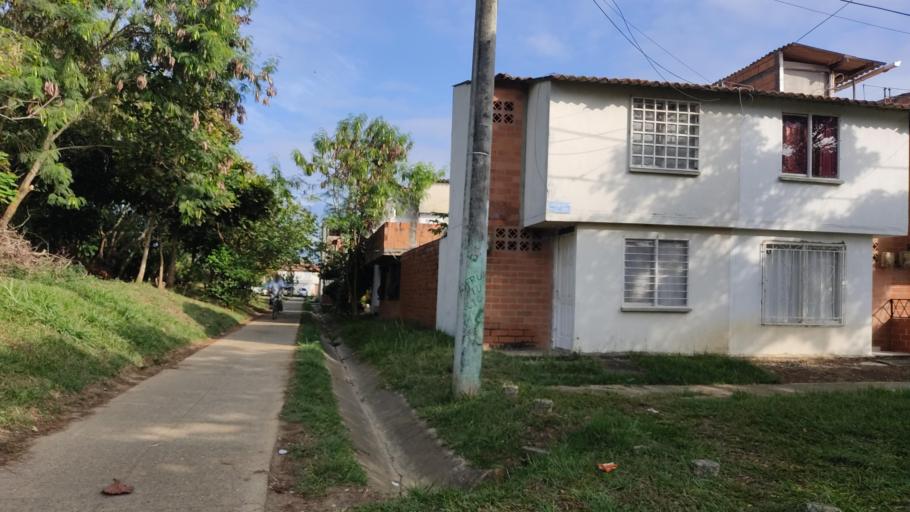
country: CO
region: Valle del Cauca
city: Jamundi
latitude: 3.2390
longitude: -76.5133
